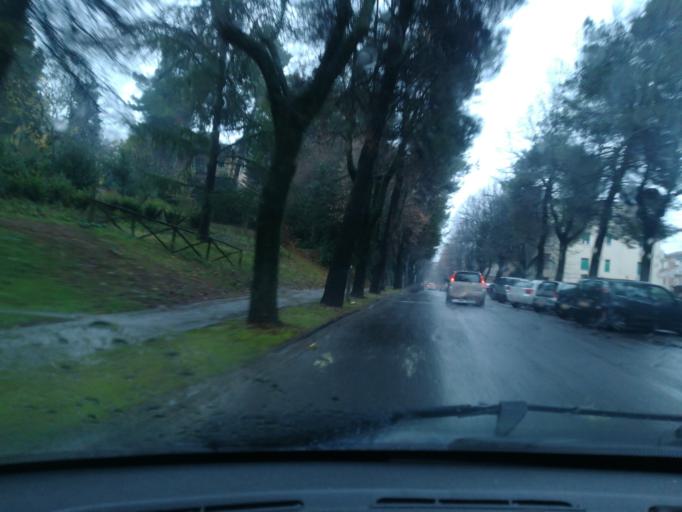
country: IT
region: The Marches
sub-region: Provincia di Macerata
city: Macerata
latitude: 43.2970
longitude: 13.4369
